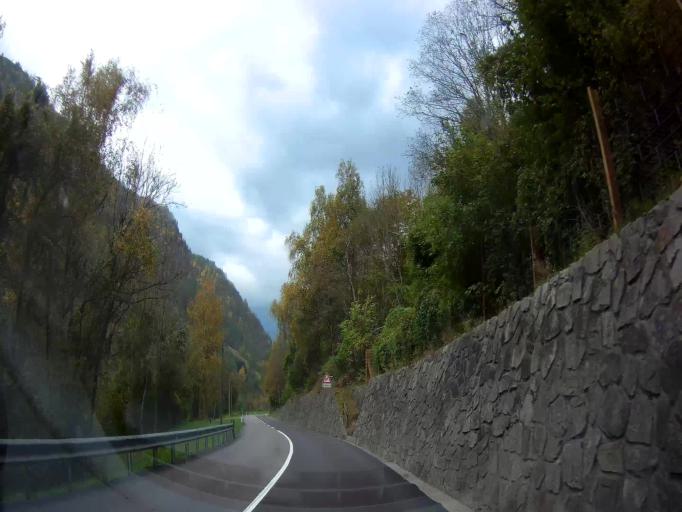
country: IT
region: Trentino-Alto Adige
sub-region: Bolzano
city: Certosa
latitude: 46.6824
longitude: 10.9347
